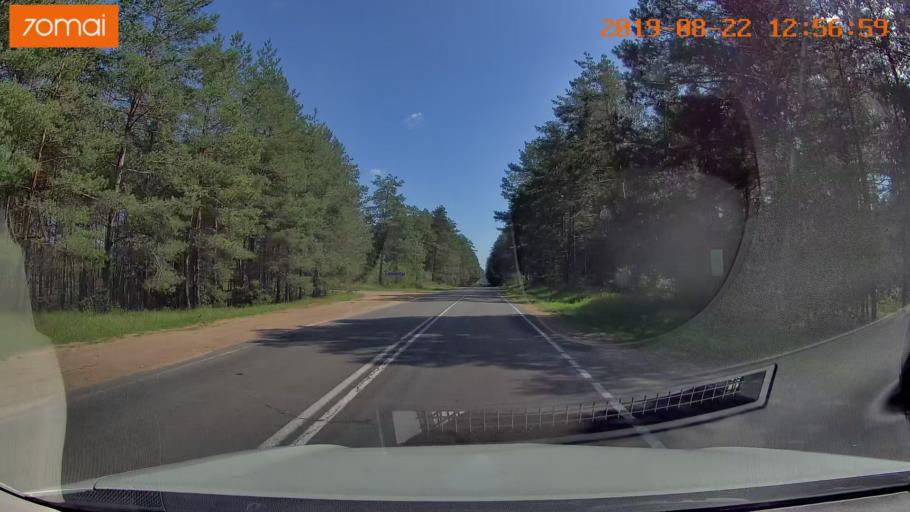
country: BY
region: Minsk
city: Prawdzinski
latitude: 53.4309
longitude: 27.7400
